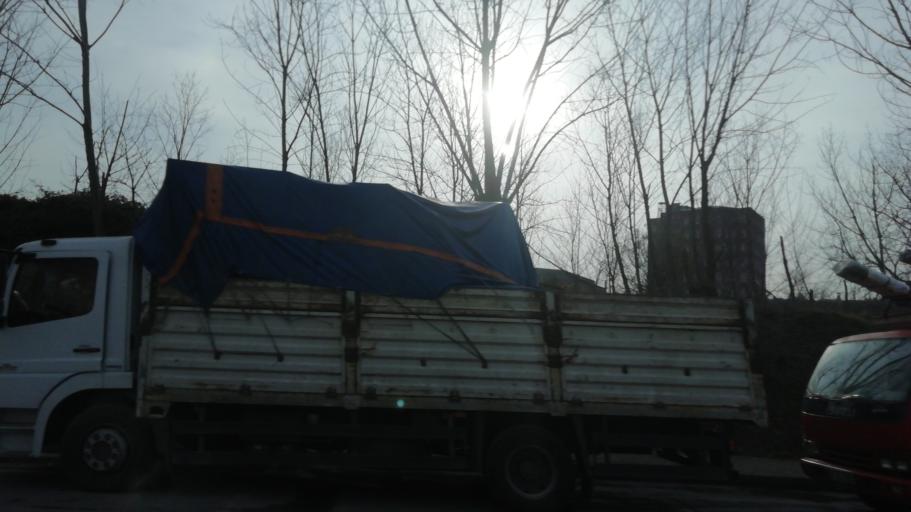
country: TR
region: Istanbul
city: Basaksehir
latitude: 41.0844
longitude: 28.8090
